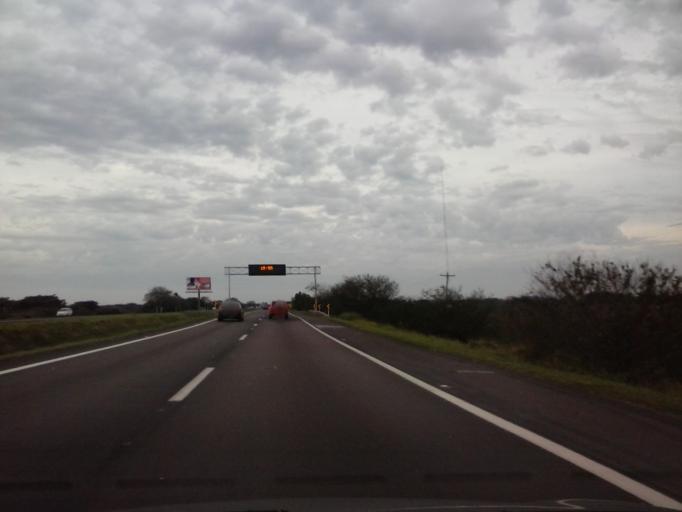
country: BR
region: Rio Grande do Sul
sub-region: Porto Alegre
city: Porto Alegre
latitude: -29.9983
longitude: -51.2923
